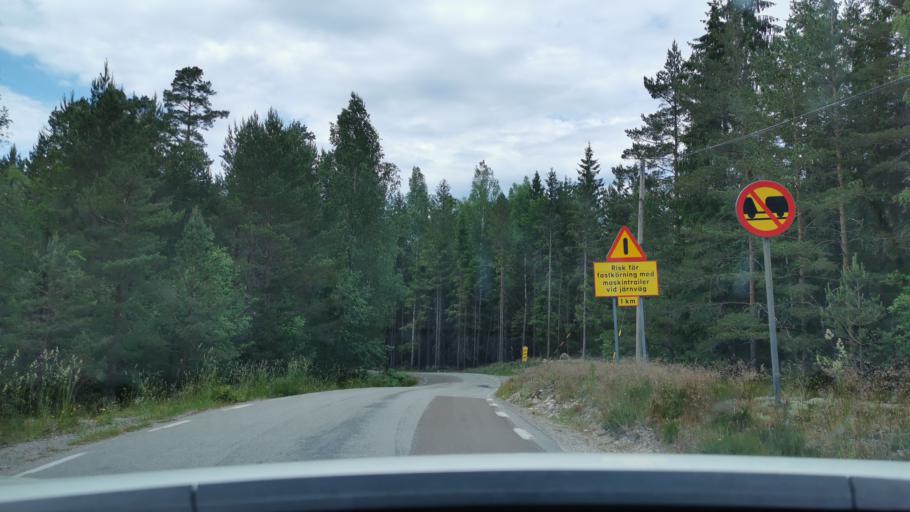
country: SE
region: Vaestra Goetaland
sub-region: Bengtsfors Kommun
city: Dals Langed
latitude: 58.8341
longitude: 12.4121
